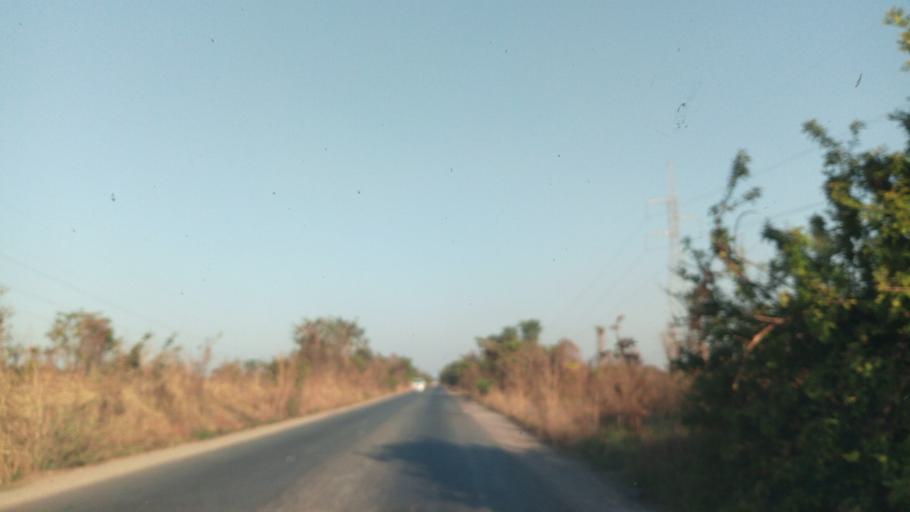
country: CD
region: Katanga
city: Likasi
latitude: -11.1154
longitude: 27.0269
